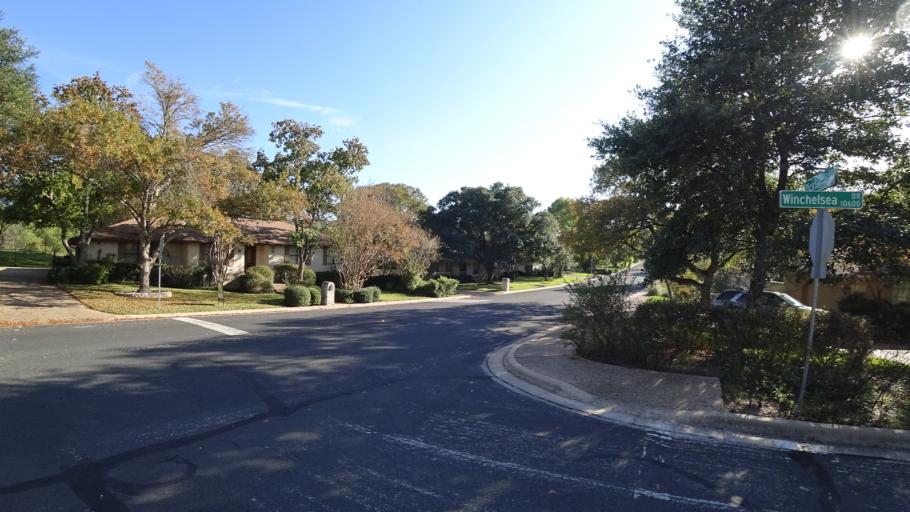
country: US
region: Texas
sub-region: Williamson County
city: Anderson Mill
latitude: 30.4347
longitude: -97.8099
